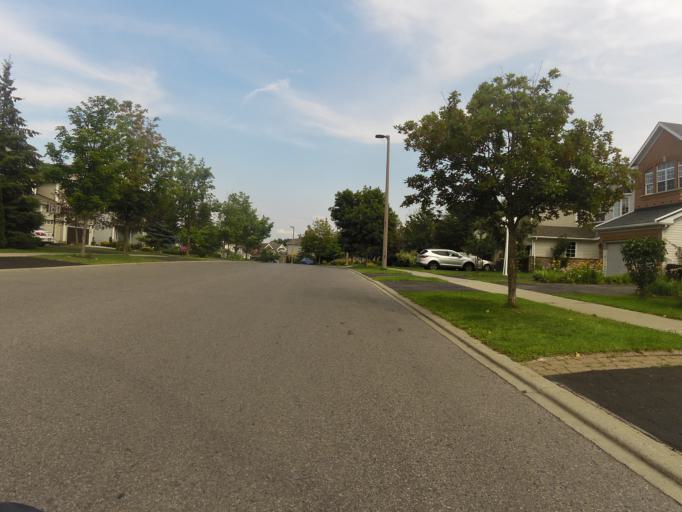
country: CA
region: Ontario
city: Bells Corners
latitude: 45.3119
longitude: -75.9257
